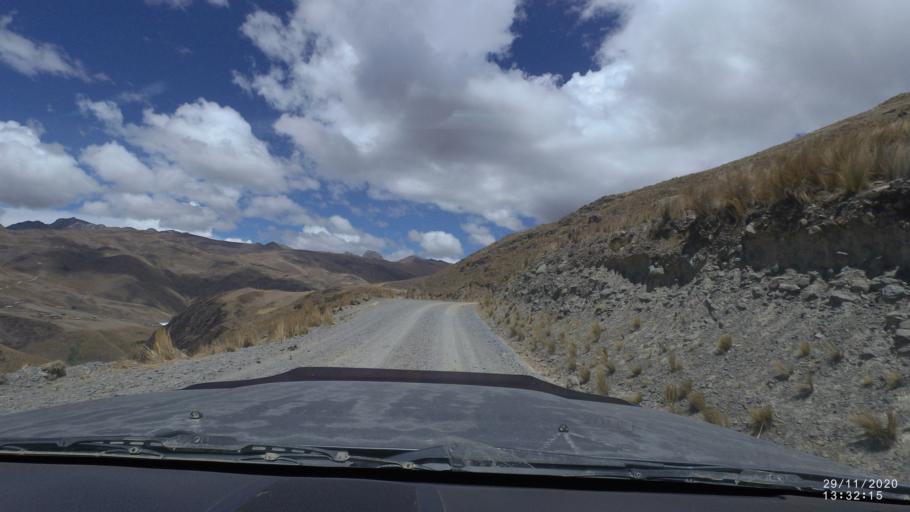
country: BO
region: Cochabamba
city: Cochabamba
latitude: -17.1069
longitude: -66.3429
